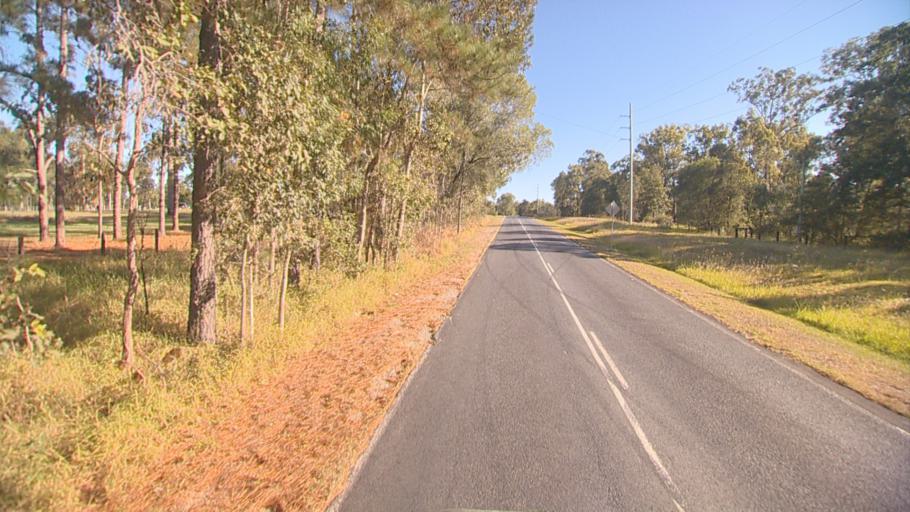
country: AU
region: Queensland
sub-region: Logan
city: North Maclean
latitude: -27.7867
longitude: 153.0468
